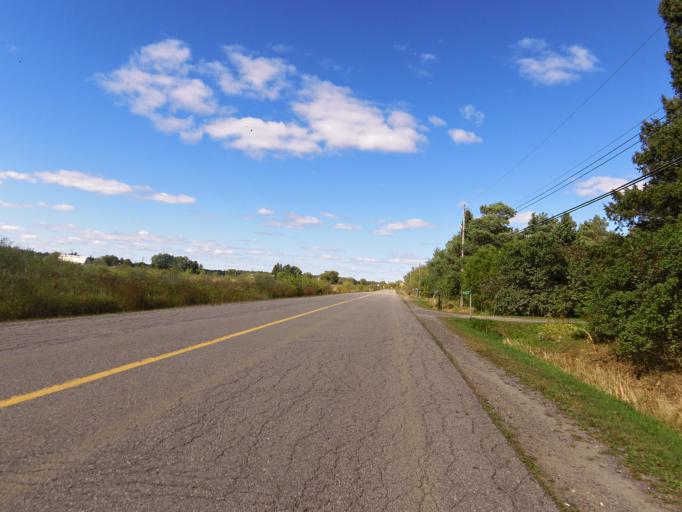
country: CA
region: Ontario
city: Ottawa
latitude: 45.3302
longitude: -75.4908
